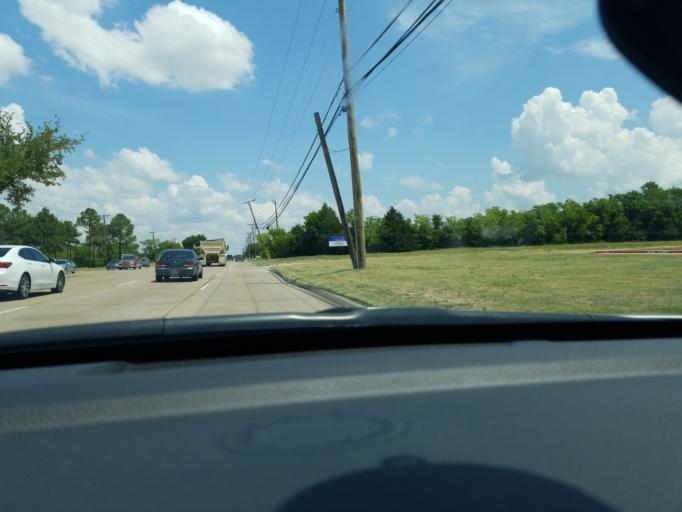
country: US
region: Texas
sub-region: Dallas County
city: Mesquite
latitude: 32.8014
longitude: -96.5957
